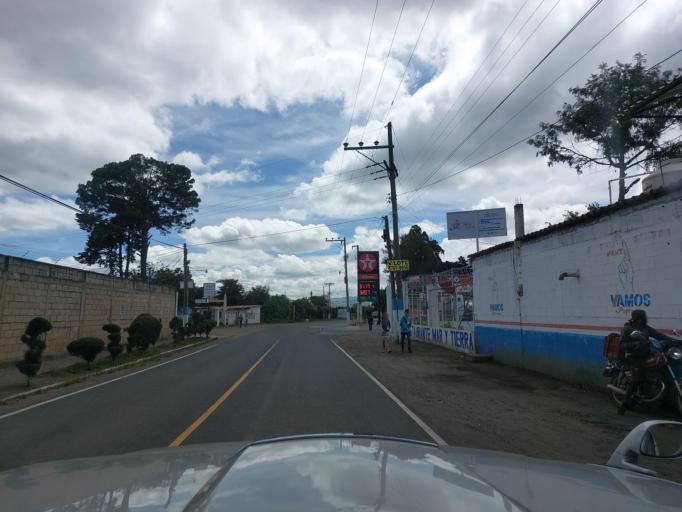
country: GT
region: Chimaltenango
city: Parramos
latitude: 14.6102
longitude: -90.7969
